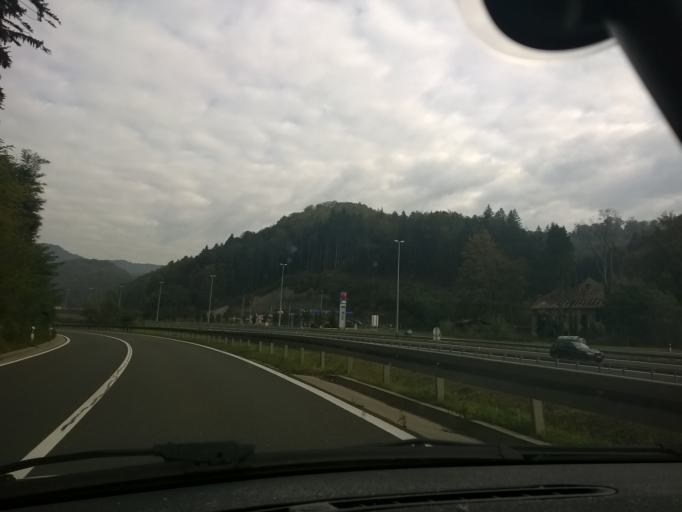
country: SI
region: Zetale
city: Zetale
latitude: 46.2374
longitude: 15.8463
